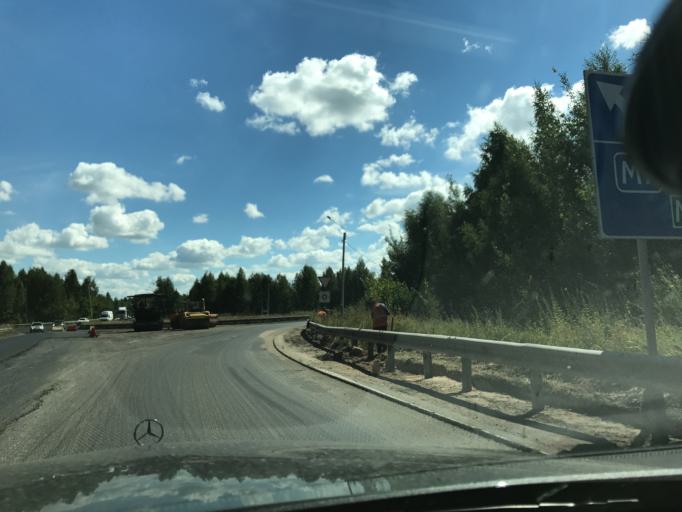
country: RU
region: Nizjnij Novgorod
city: Gorbatovka
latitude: 56.2195
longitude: 43.7548
